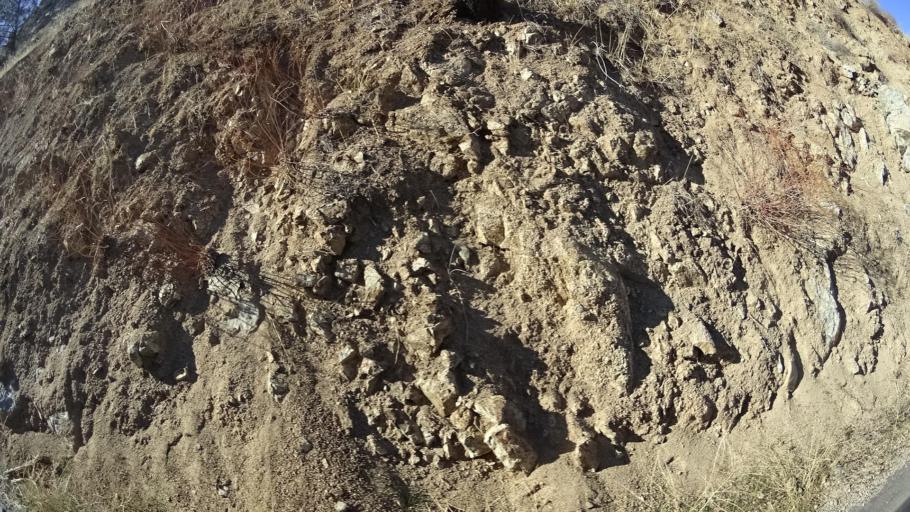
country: US
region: California
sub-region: Kern County
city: Bodfish
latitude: 35.5831
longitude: -118.5021
